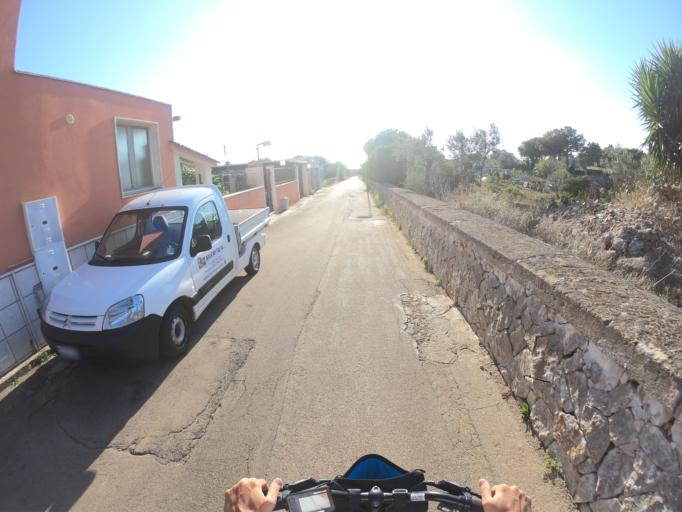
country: IT
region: Apulia
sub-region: Provincia di Lecce
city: Parabita
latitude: 40.0549
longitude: 18.1461
